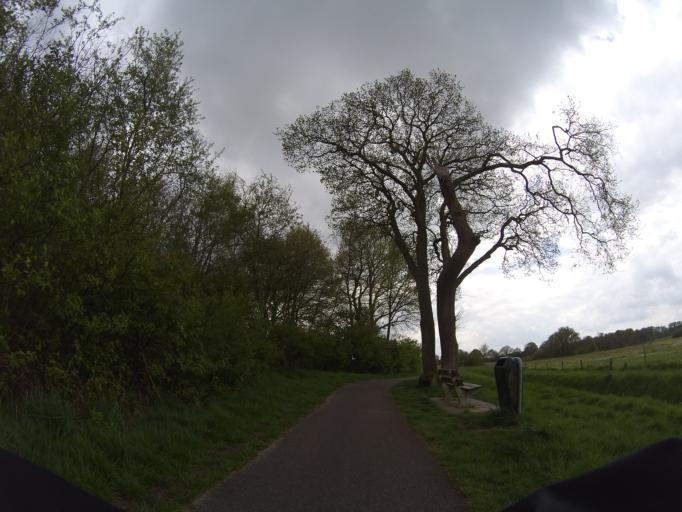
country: NL
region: Overijssel
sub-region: Gemeente Hardenberg
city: Hardenberg
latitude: 52.5573
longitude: 6.6021
